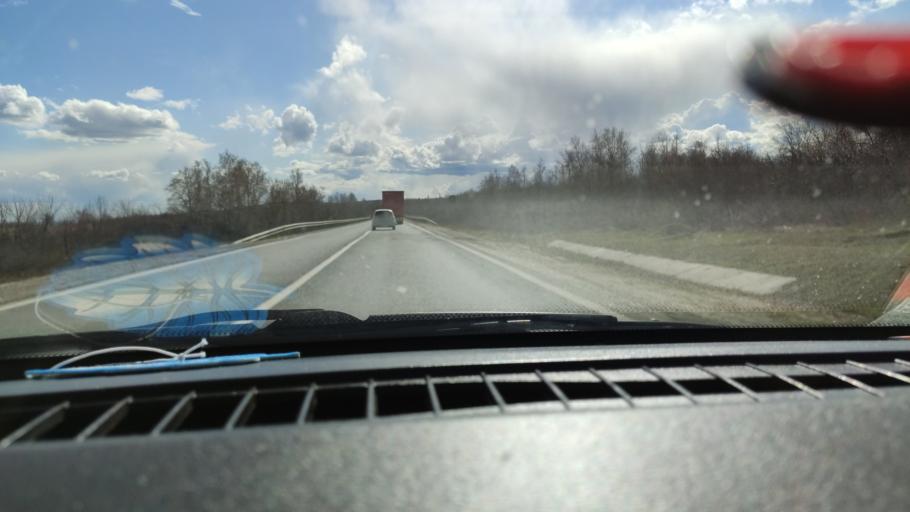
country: RU
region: Saratov
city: Dukhovnitskoye
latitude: 52.6754
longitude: 48.2266
